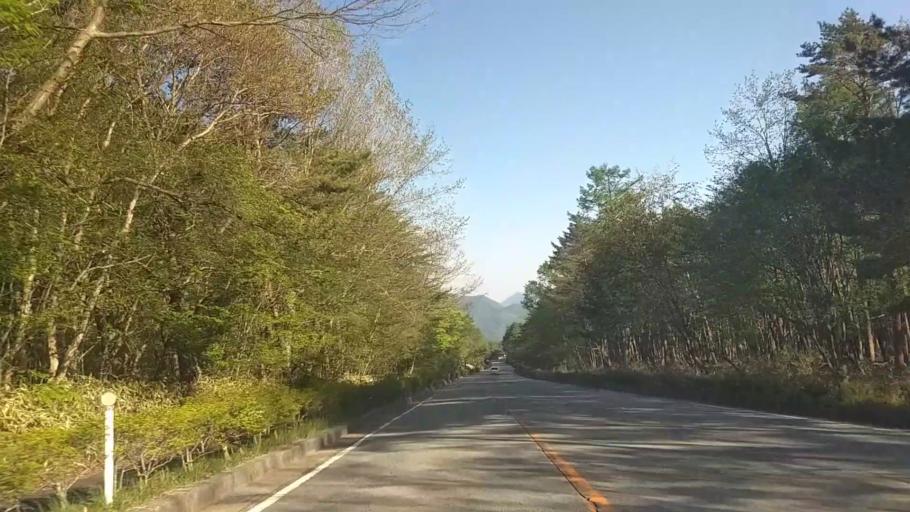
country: JP
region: Yamanashi
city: Nirasaki
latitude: 35.9292
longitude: 138.4290
